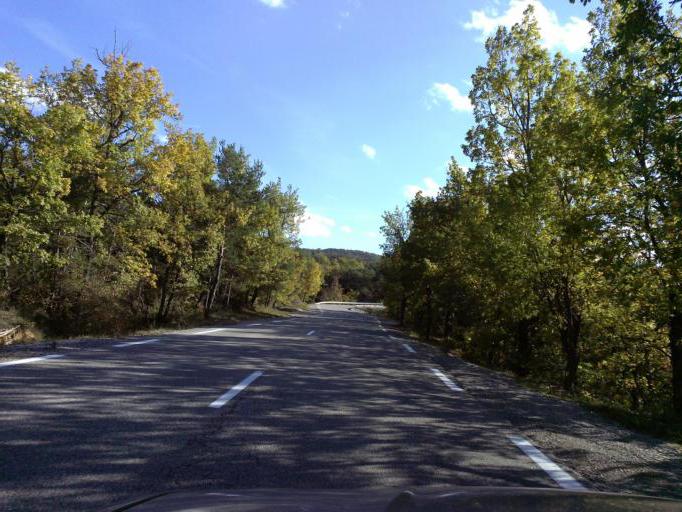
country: FR
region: Provence-Alpes-Cote d'Azur
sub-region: Departement des Alpes-de-Haute-Provence
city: Riez
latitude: 43.9137
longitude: 6.1380
